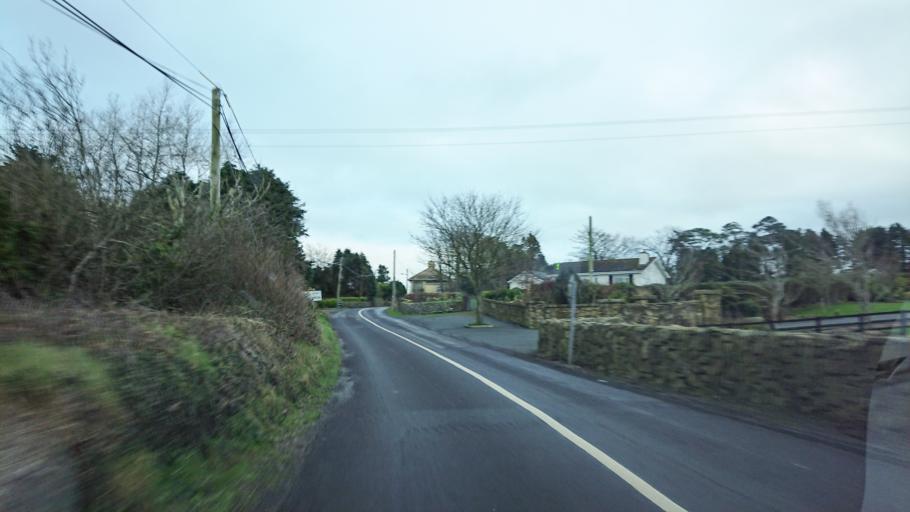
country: IE
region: Munster
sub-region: Waterford
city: Portlaw
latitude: 52.1729
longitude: -7.4021
